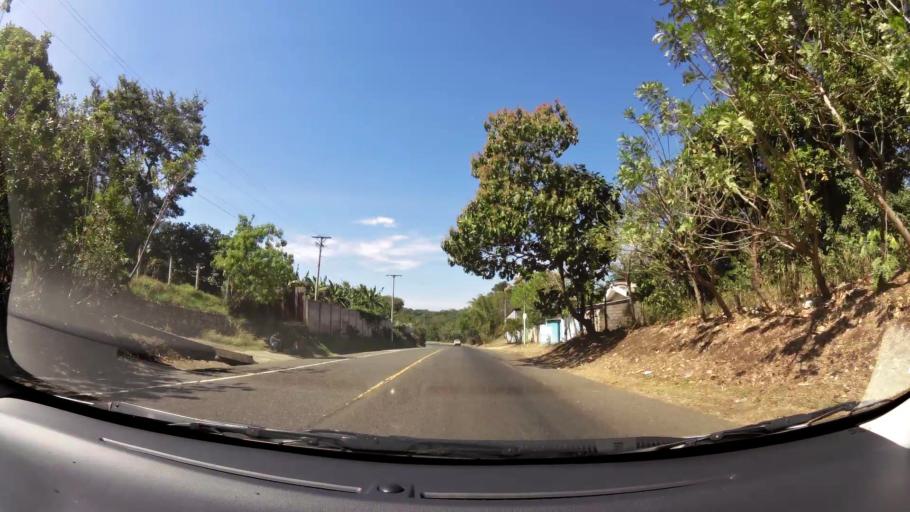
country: SV
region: Ahuachapan
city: Ahuachapan
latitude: 13.9517
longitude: -89.8189
